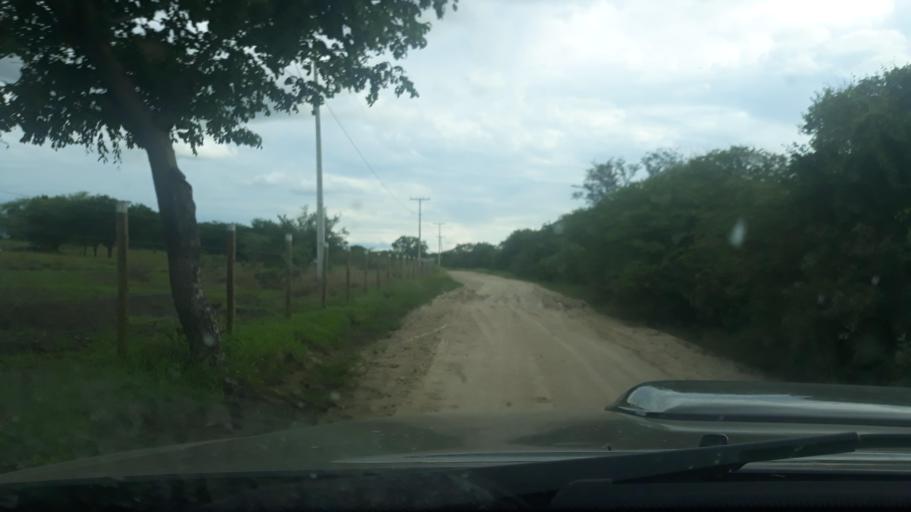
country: BR
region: Bahia
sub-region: Riacho De Santana
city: Riacho de Santana
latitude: -13.8800
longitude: -43.0209
